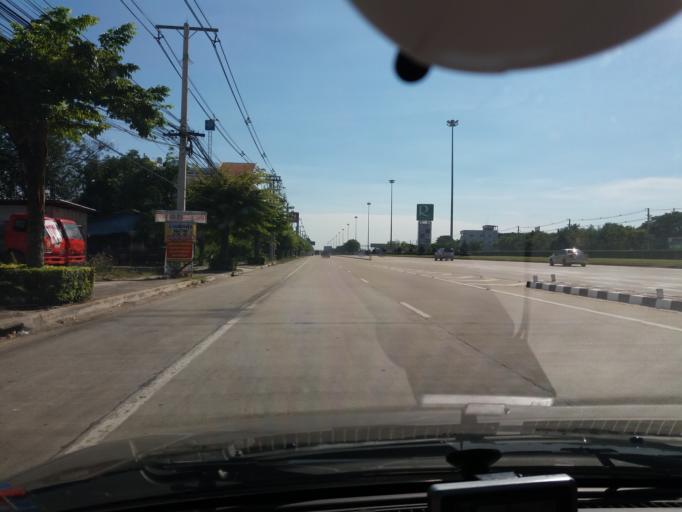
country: TH
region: Suphan Buri
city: Suphan Buri
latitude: 14.4624
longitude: 100.1317
